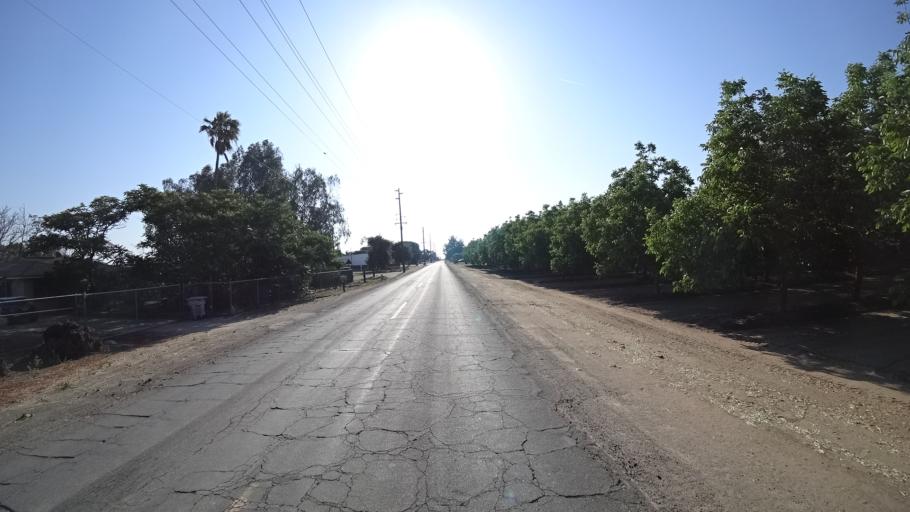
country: US
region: California
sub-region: Kings County
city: Home Garden
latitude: 36.3135
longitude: -119.5802
